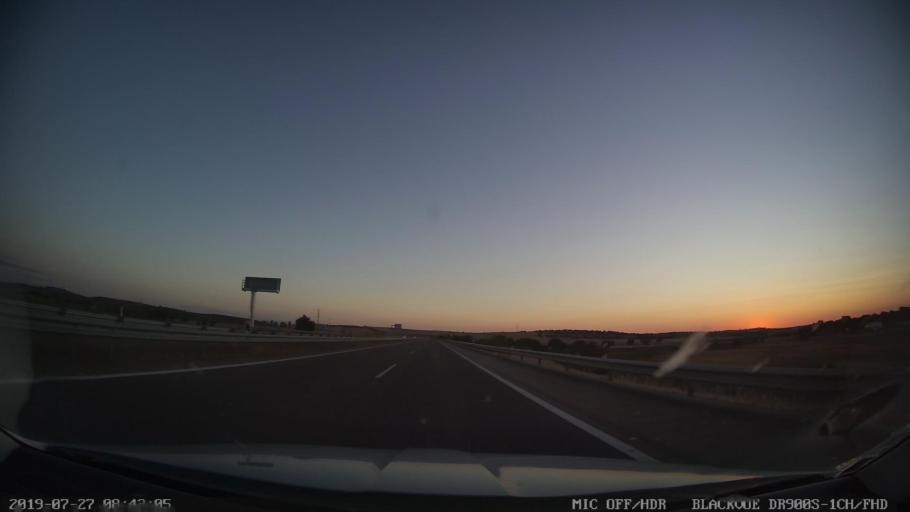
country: ES
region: Extremadura
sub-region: Provincia de Badajoz
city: Badajoz
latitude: 38.9191
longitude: -6.9742
